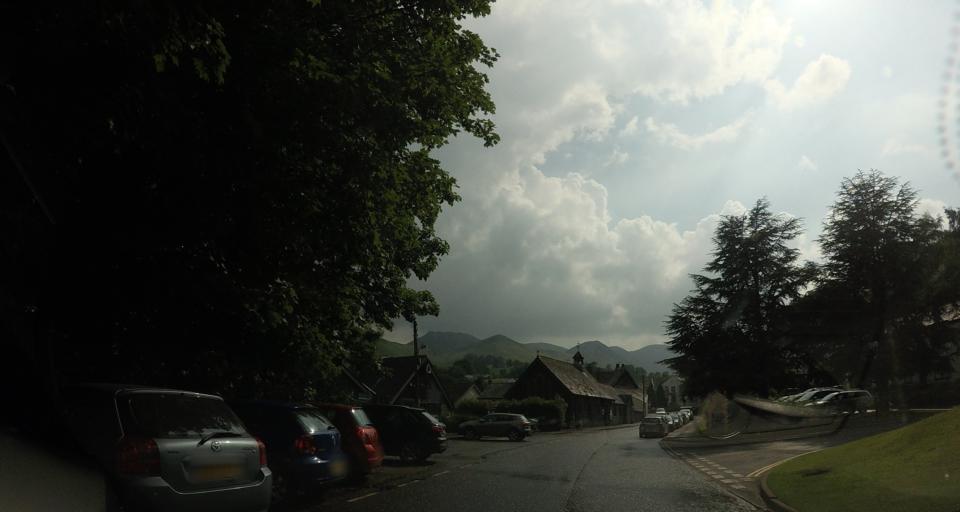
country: GB
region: England
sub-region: Cumbria
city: Keswick
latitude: 54.6032
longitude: -3.1896
